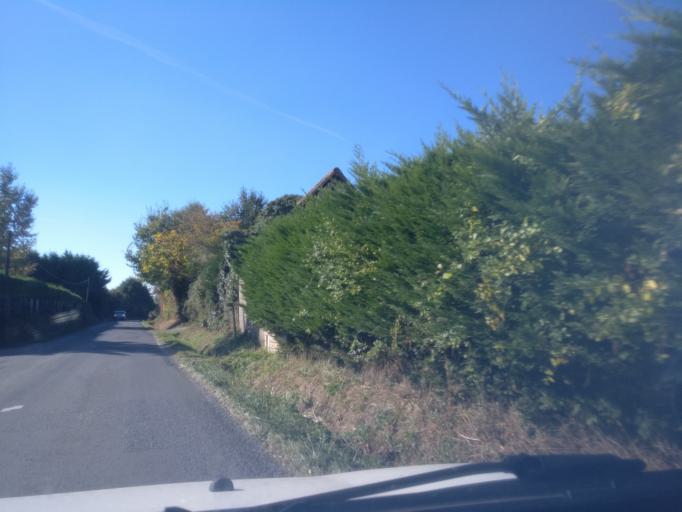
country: FR
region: Brittany
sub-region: Departement d'Ille-et-Vilaine
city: Melesse
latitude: 48.2132
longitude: -1.6707
